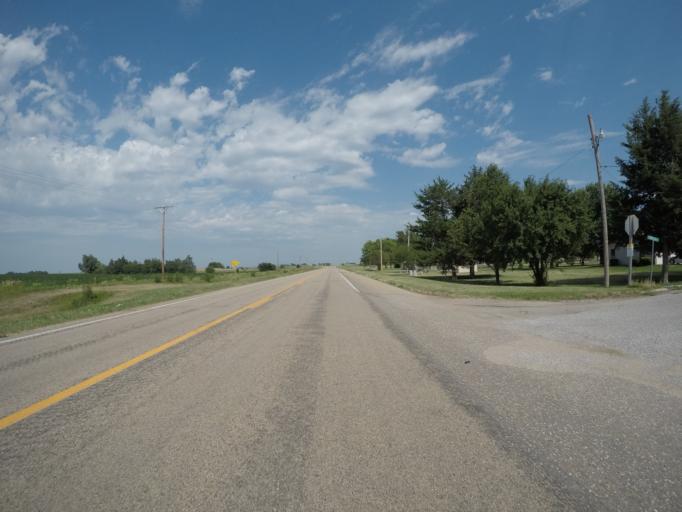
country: US
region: Nebraska
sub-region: Thayer County
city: Hebron
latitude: 40.0166
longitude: -97.6174
